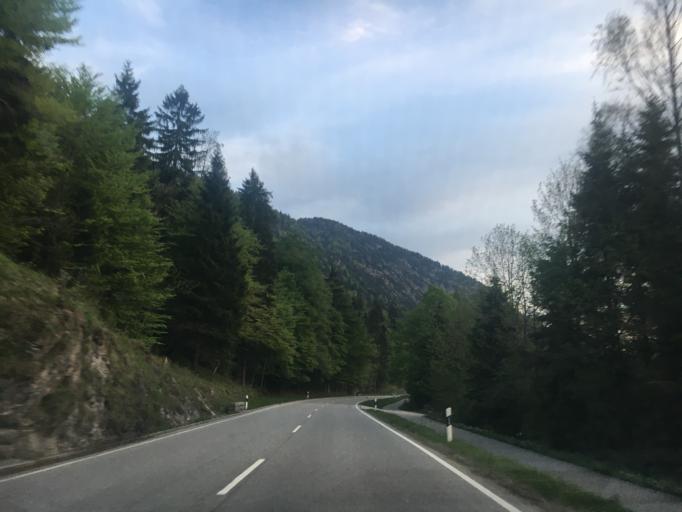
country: DE
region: Bavaria
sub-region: Upper Bavaria
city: Lenggries
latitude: 47.6107
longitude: 11.5846
